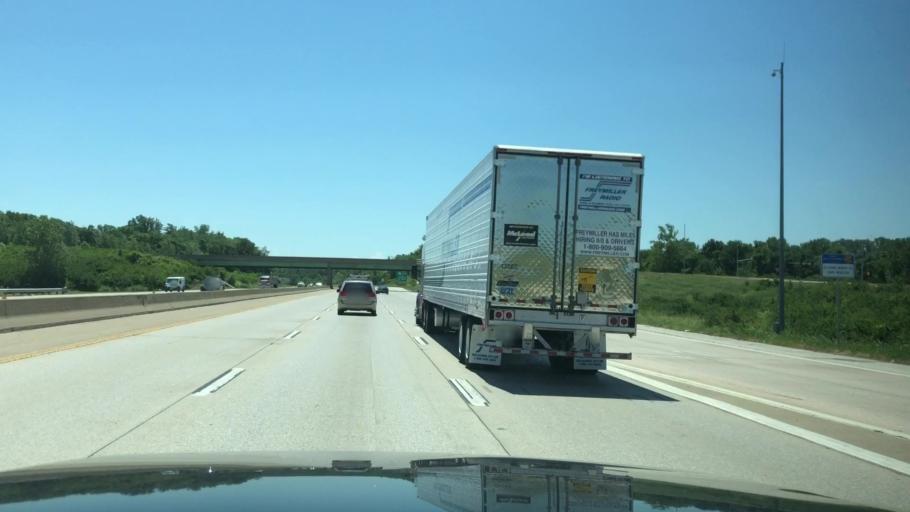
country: US
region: Missouri
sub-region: Saint Louis County
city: Bridgeton
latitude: 38.7825
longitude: -90.4178
